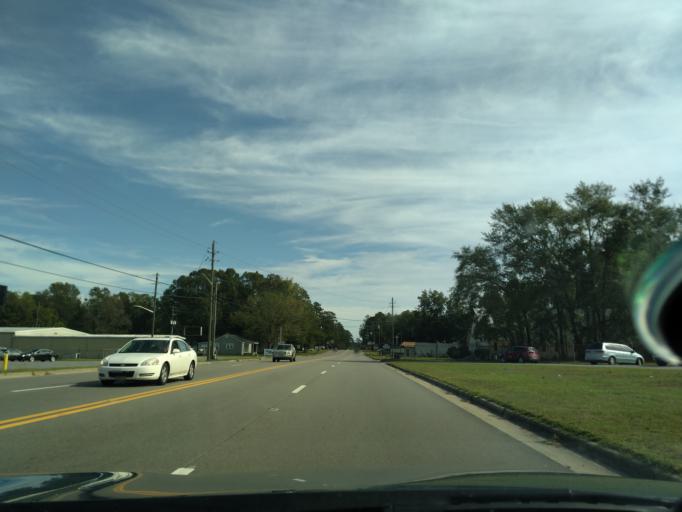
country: US
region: North Carolina
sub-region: Beaufort County
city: Washington
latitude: 35.5337
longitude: -77.0230
